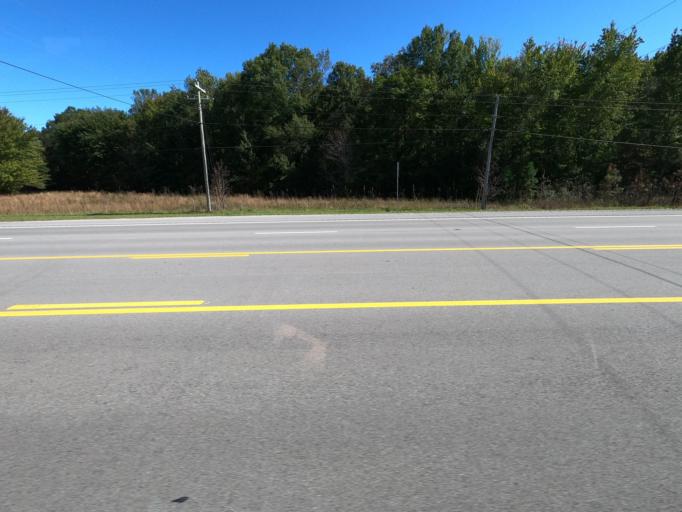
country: US
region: Tennessee
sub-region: Maury County
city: Mount Pleasant
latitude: 35.4380
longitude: -87.2800
